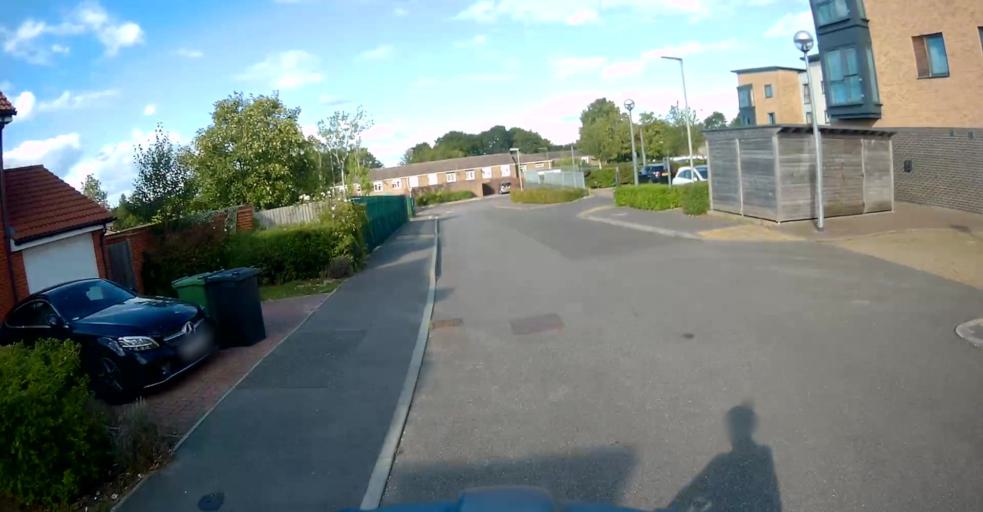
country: GB
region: England
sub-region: Hampshire
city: Basingstoke
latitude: 51.2440
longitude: -1.1187
